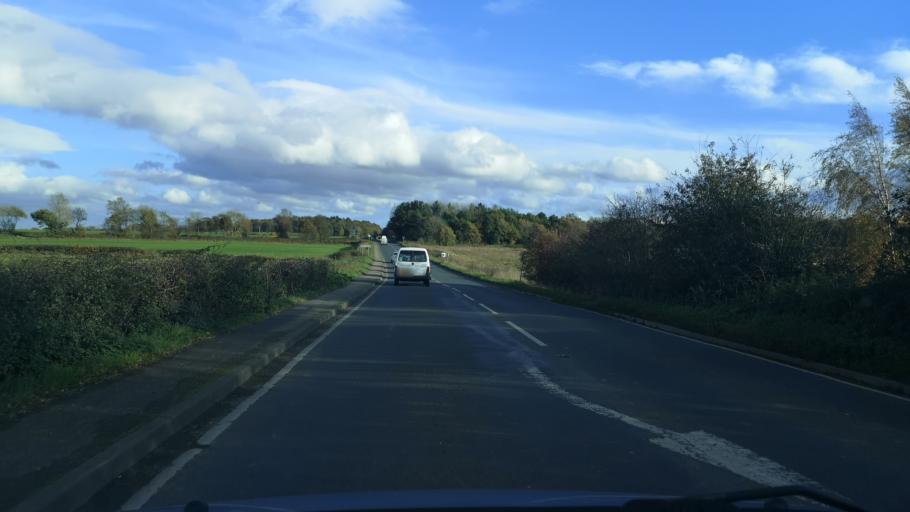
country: GB
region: England
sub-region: City and Borough of Wakefield
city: Middlestown
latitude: 53.6271
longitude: -1.5880
